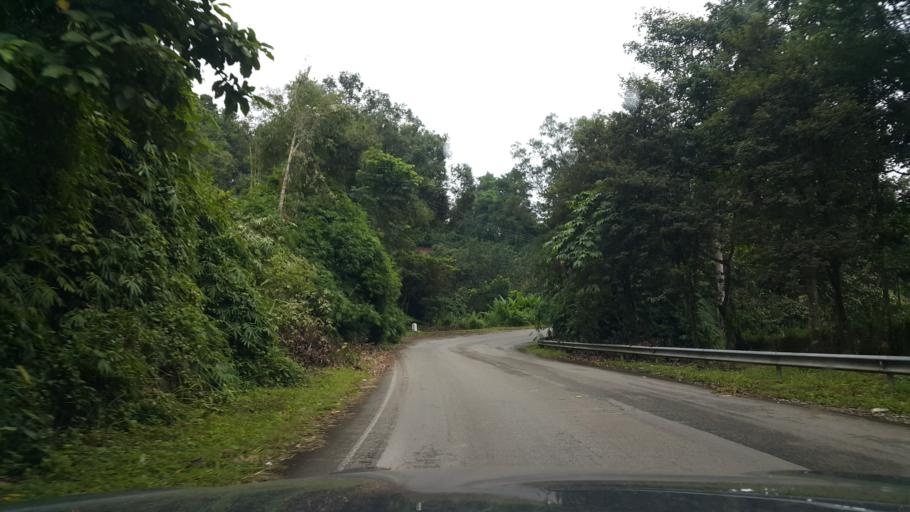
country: TH
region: Chiang Mai
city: Samoeng
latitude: 18.8100
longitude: 98.8178
